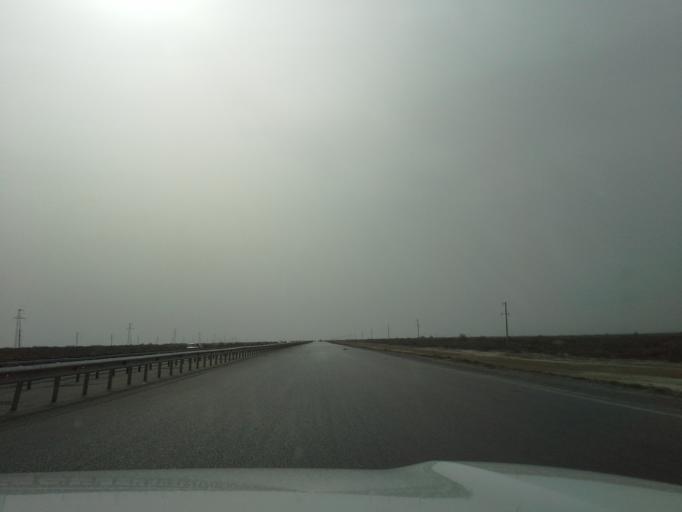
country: TM
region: Ahal
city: Kaka
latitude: 37.5041
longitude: 59.4503
